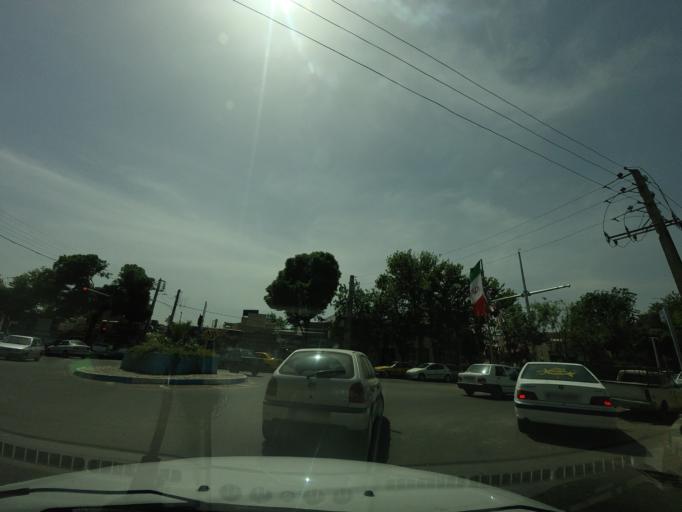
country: IR
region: Tehran
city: Eslamshahr
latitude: 35.6051
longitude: 51.2700
